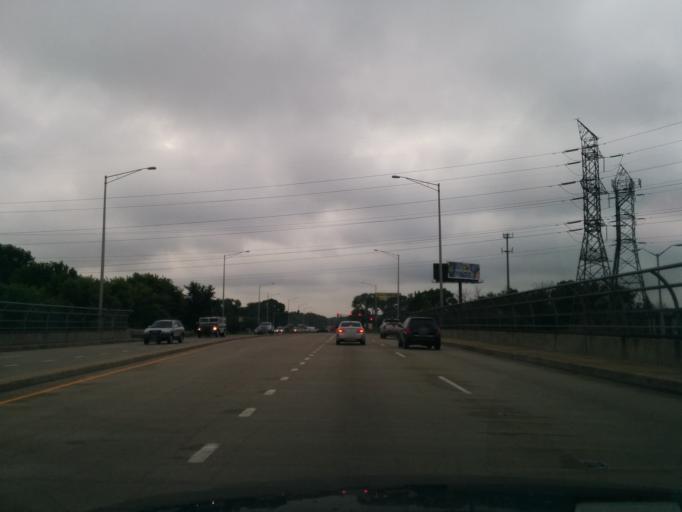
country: US
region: Illinois
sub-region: DuPage County
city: Addison
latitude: 41.9242
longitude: -87.9664
